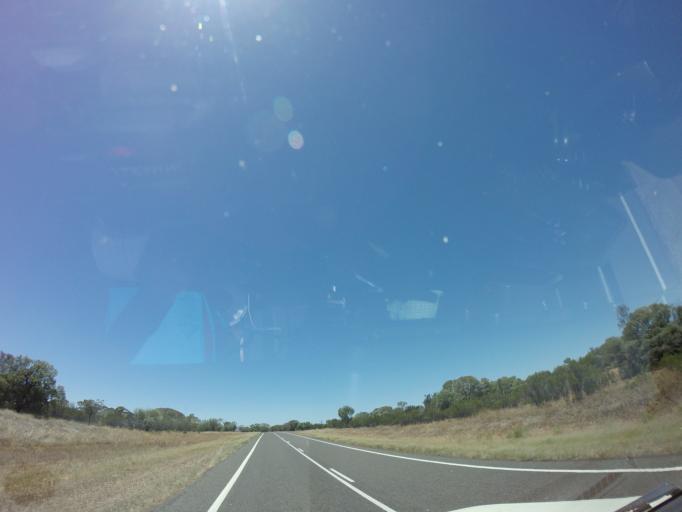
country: AU
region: New South Wales
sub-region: Cobar
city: Cobar
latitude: -31.5745
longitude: 144.7985
